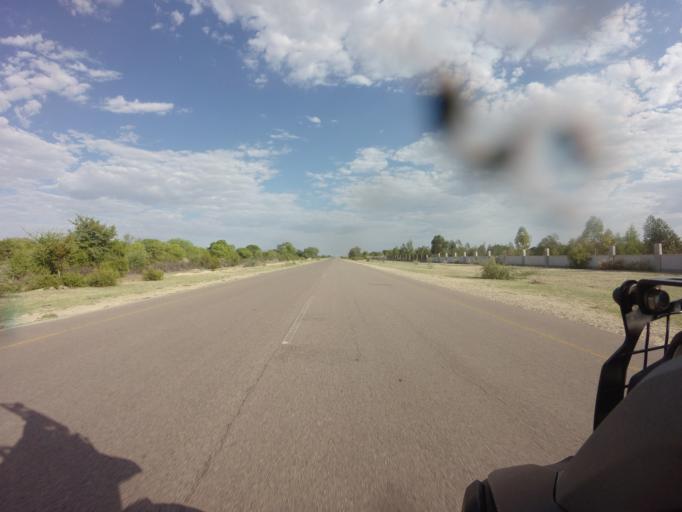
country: AO
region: Cunene
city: Ondjiva
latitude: -17.0009
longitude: 15.6381
